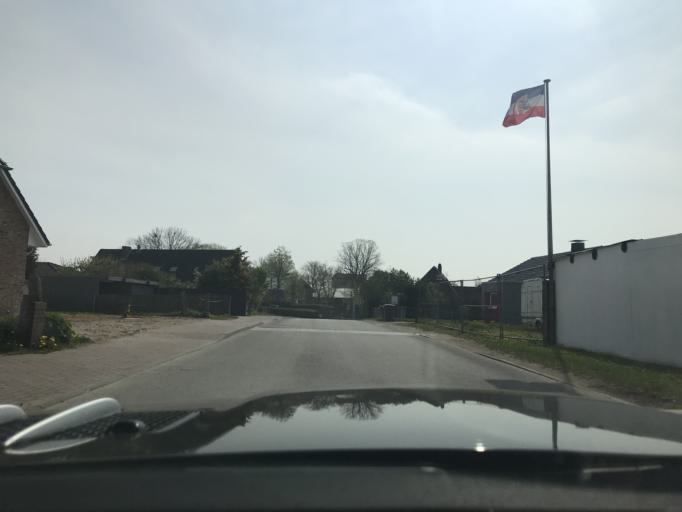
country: DE
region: Schleswig-Holstein
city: Gromitz
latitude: 54.1673
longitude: 10.9810
